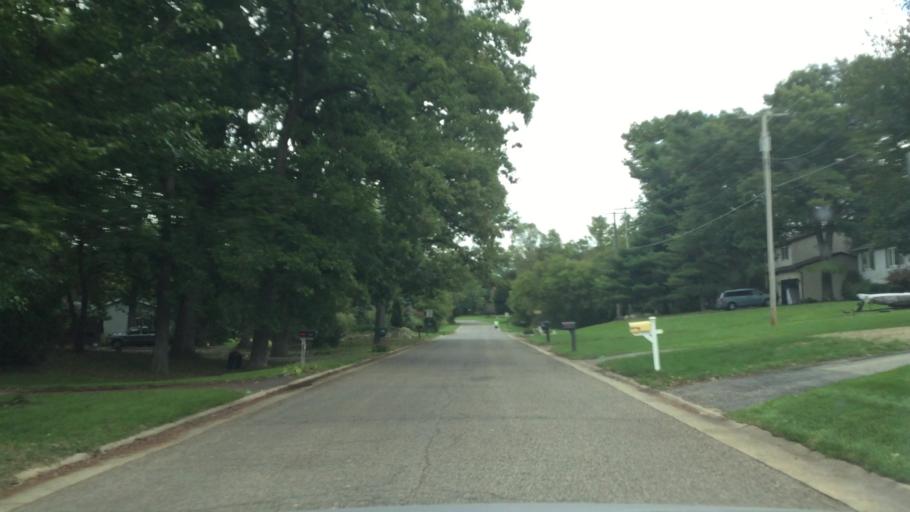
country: US
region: Michigan
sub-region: Livingston County
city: Brighton
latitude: 42.5568
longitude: -83.7506
